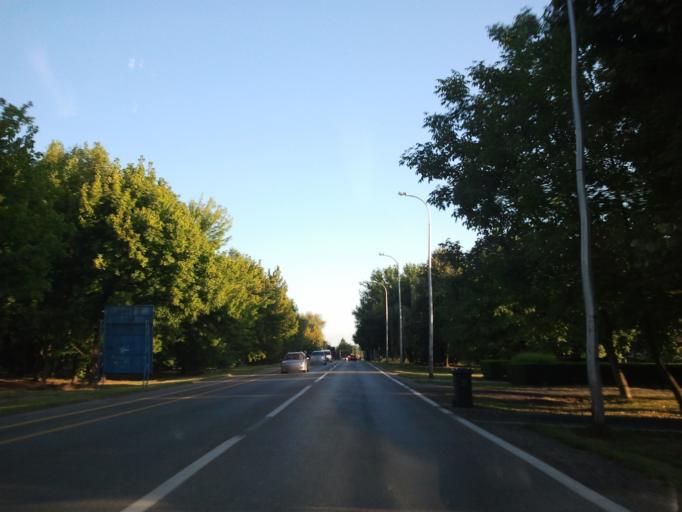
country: HR
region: Sisacko-Moslavacka
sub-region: Grad Sisak
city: Sisak
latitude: 45.4572
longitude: 16.3713
